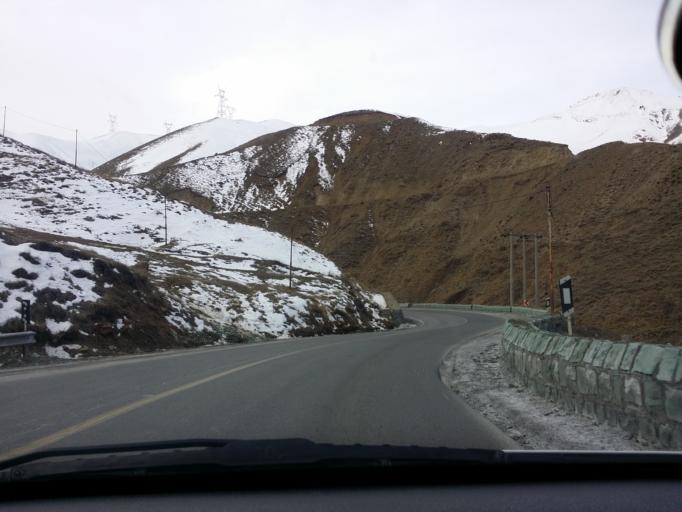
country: IR
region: Tehran
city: Tajrish
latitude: 36.1769
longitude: 51.3156
